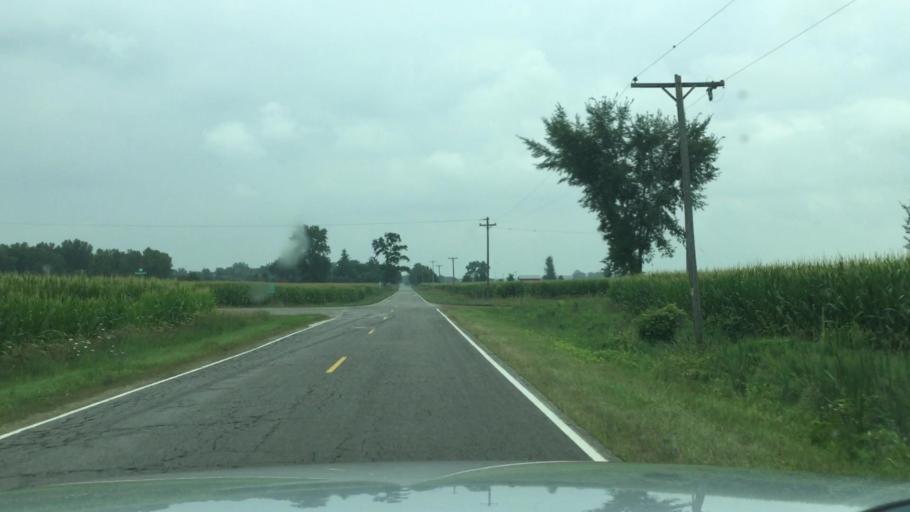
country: US
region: Michigan
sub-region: Shiawassee County
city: New Haven
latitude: 43.0870
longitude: -84.2262
